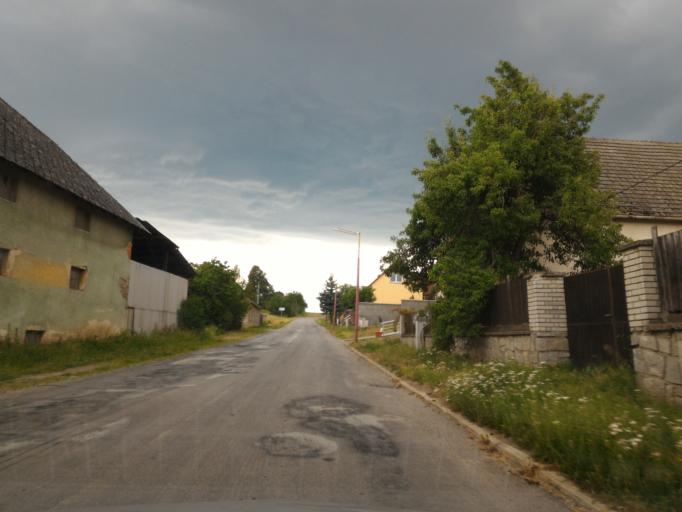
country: CZ
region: Vysocina
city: Zeletava
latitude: 49.1182
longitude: 15.6153
